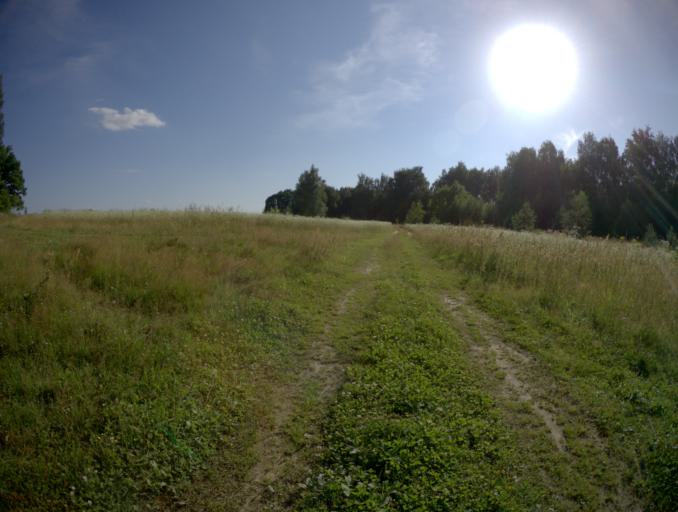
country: RU
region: Vladimir
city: Bogolyubovo
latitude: 56.1207
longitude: 40.5348
